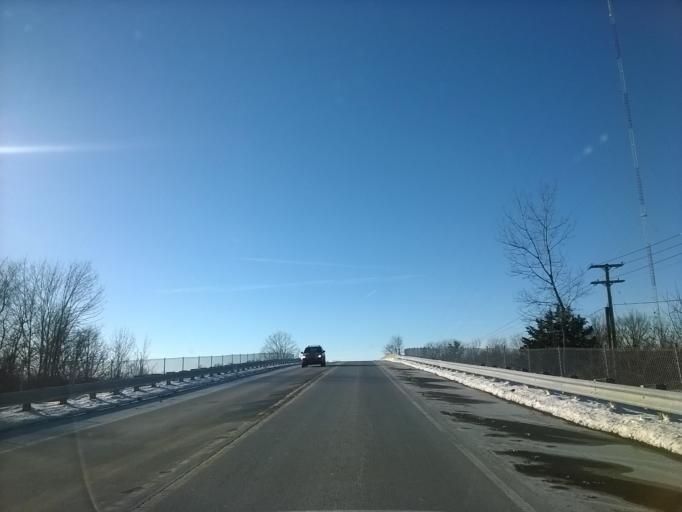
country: US
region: Indiana
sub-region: Marion County
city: Meridian Hills
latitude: 39.9269
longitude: -86.1771
